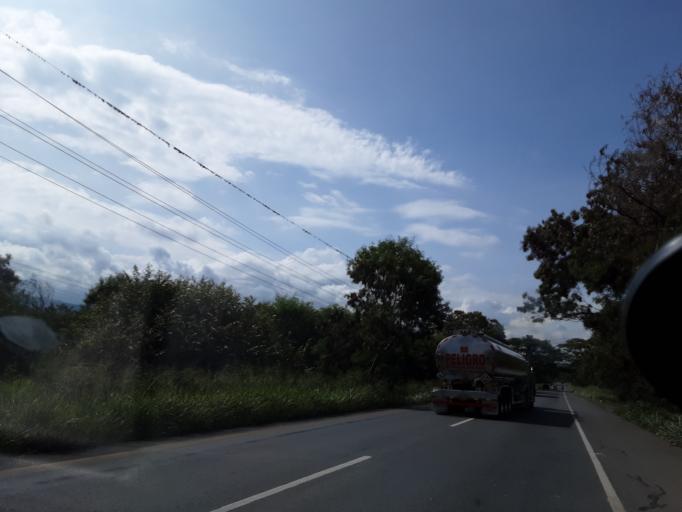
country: CO
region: Valle del Cauca
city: Buga
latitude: 3.8715
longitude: -76.3058
